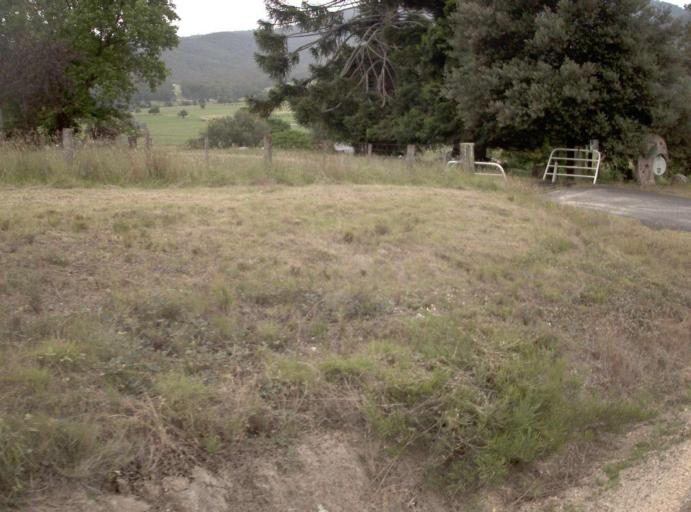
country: AU
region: New South Wales
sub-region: Bombala
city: Bombala
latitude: -37.4850
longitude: 149.1807
